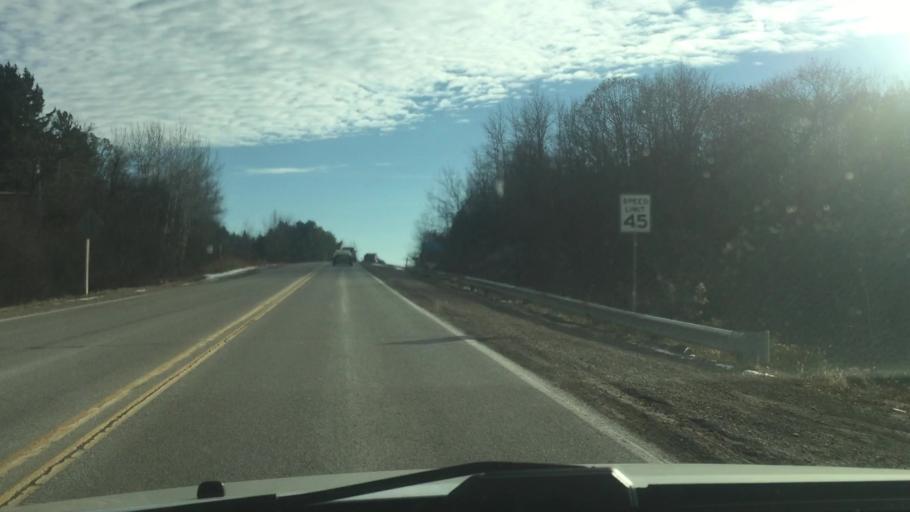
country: US
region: Wisconsin
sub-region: Waukesha County
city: Delafield
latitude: 43.0523
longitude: -88.4047
